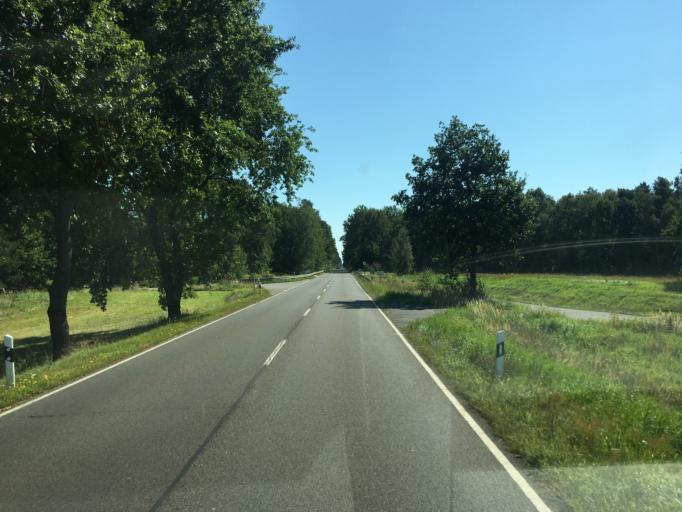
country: DE
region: Brandenburg
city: Welzow
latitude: 51.5412
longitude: 14.1811
